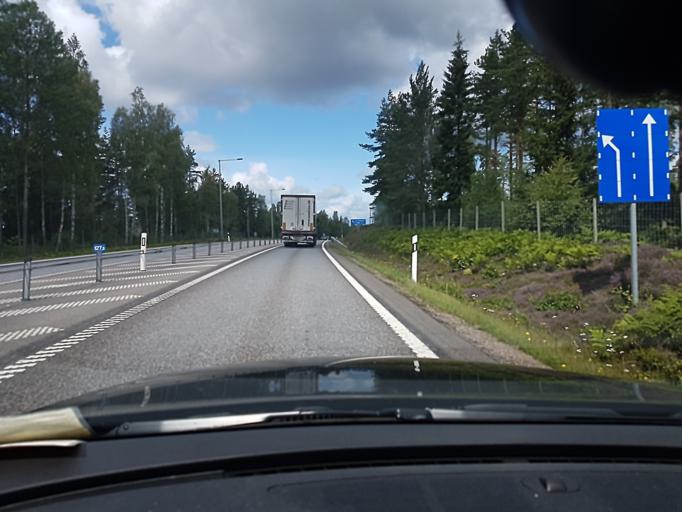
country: SE
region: Kronoberg
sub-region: Lessebo Kommun
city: Hovmantorp
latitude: 56.7945
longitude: 15.1218
